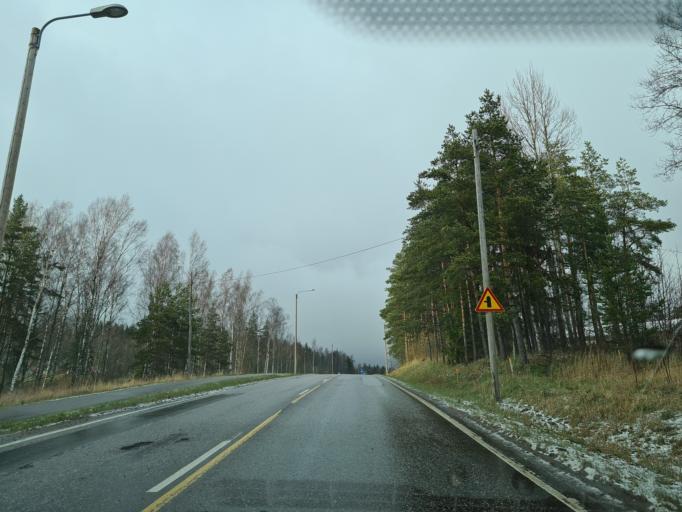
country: FI
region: Uusimaa
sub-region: Helsinki
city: Kirkkonummi
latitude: 60.0893
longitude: 24.4094
